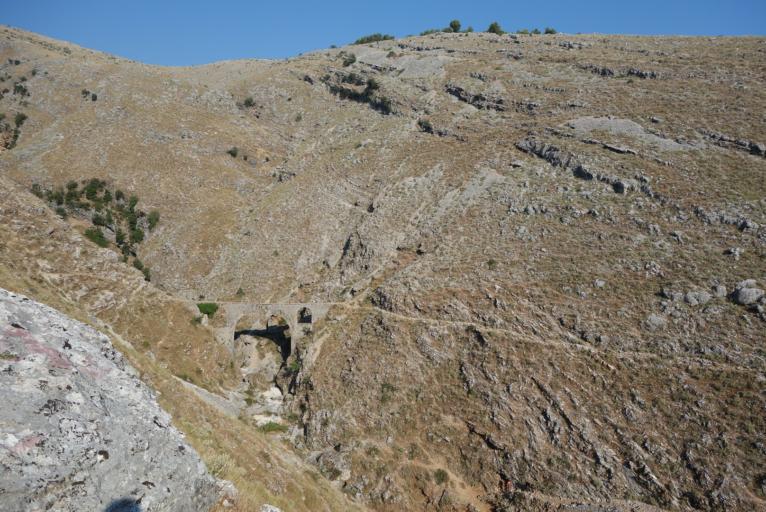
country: AL
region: Gjirokaster
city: Gjirokaster
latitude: 40.0647
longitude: 20.1334
